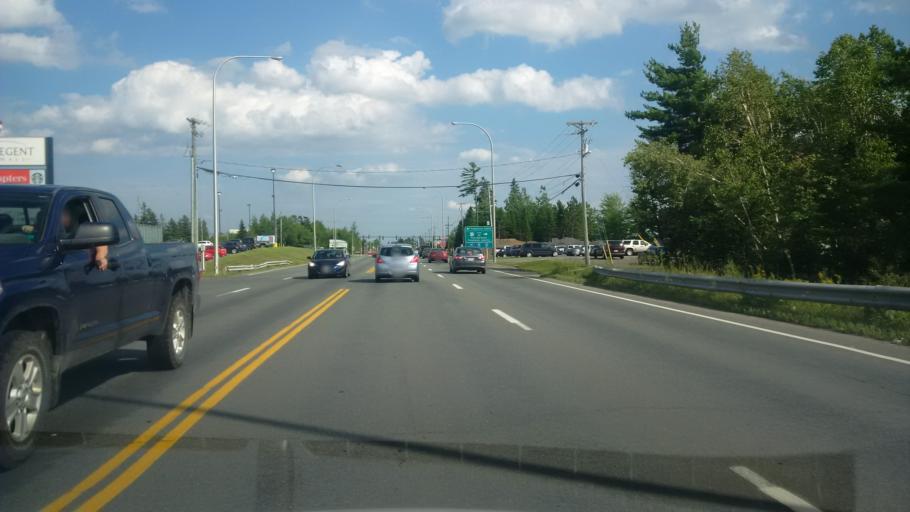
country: CA
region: New Brunswick
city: Fredericton
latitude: 45.9337
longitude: -66.6665
